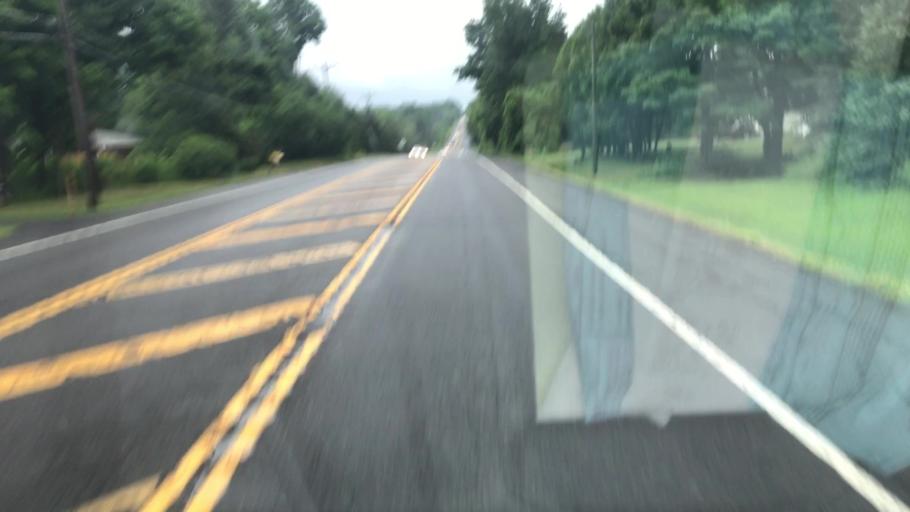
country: US
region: New York
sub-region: Onondaga County
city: Fayetteville
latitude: 43.0226
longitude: -76.0318
